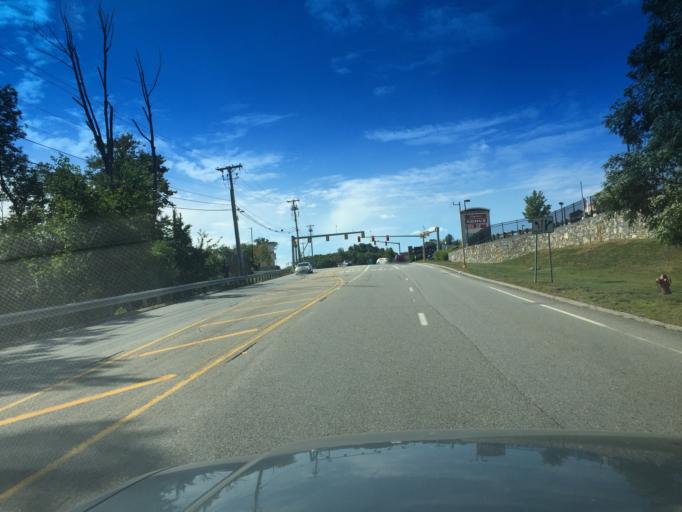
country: US
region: Massachusetts
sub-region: Worcester County
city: Northborough
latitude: 42.2869
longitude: -71.6672
